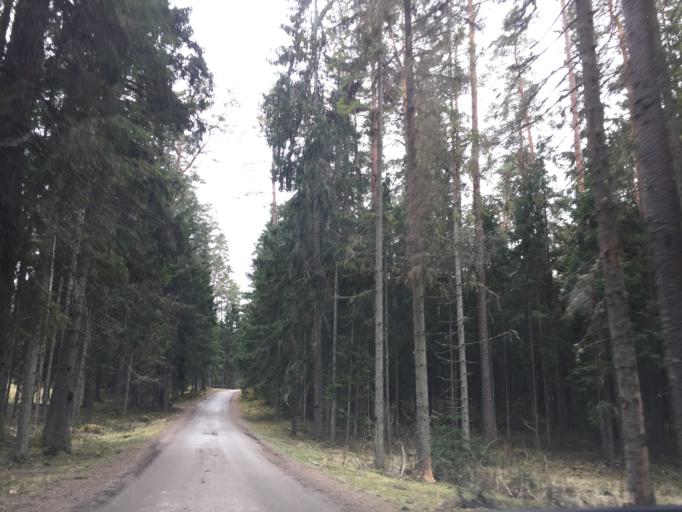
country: LV
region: Priekuli
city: Priekuli
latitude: 57.3072
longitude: 25.3857
